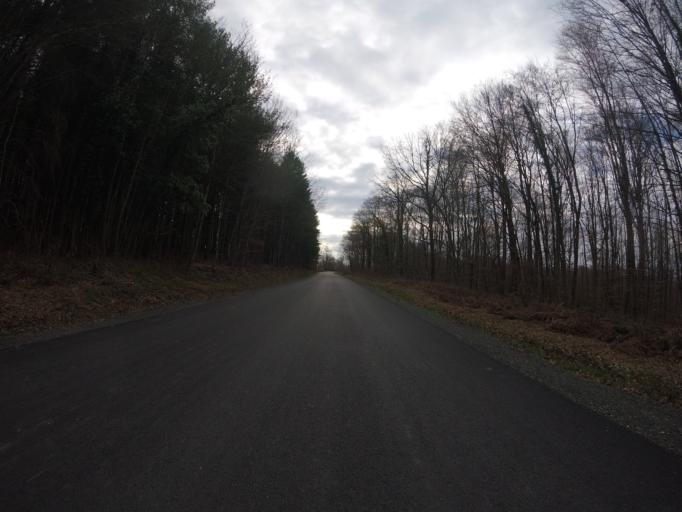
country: HR
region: Sisacko-Moslavacka
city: Glina
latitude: 45.4986
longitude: 16.0443
